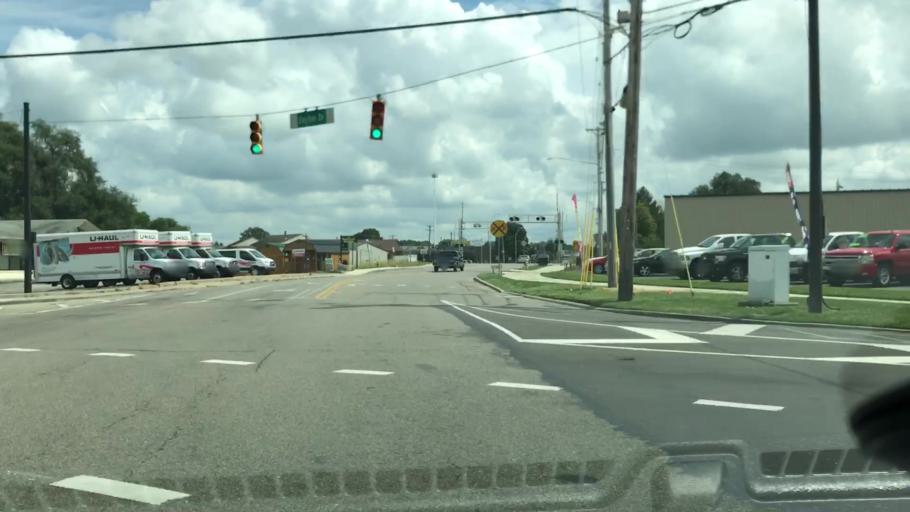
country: US
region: Ohio
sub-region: Greene County
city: Fairborn
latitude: 39.8223
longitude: -84.0148
